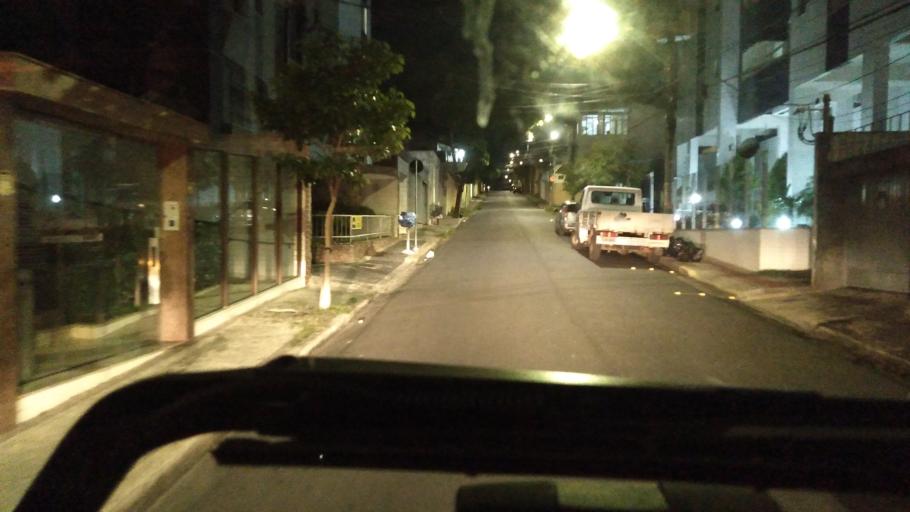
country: BR
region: Minas Gerais
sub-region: Belo Horizonte
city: Belo Horizonte
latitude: -19.9179
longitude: -43.9791
